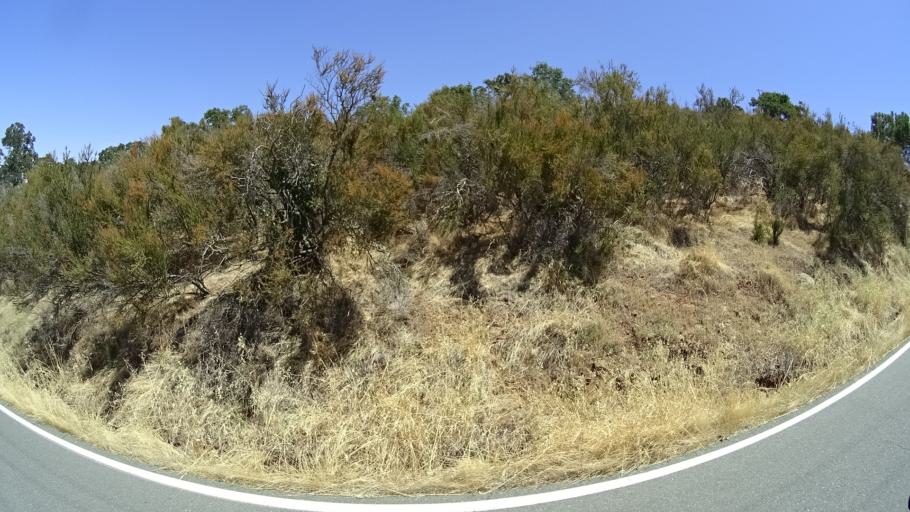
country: US
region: California
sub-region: Calaveras County
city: Rancho Calaveras
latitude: 38.1255
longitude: -120.8453
